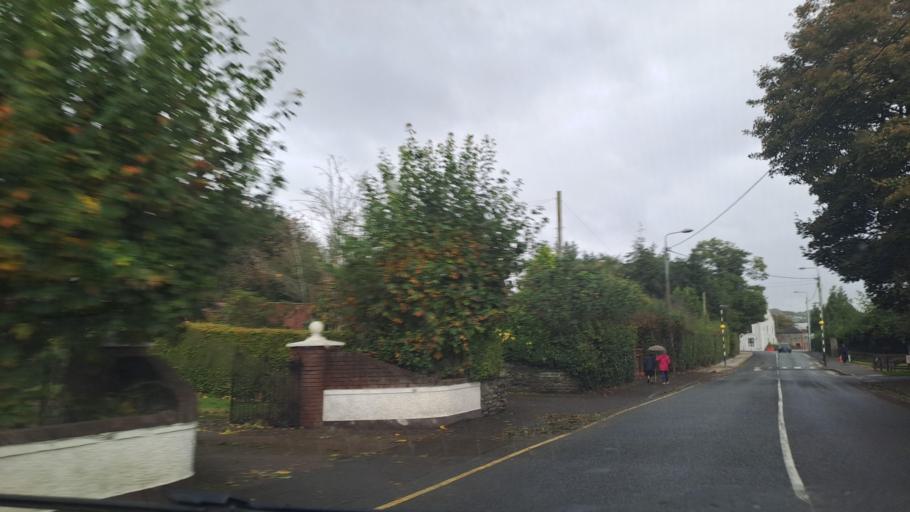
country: IE
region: Ulster
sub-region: An Cabhan
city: Bailieborough
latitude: 53.9179
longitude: -6.9760
